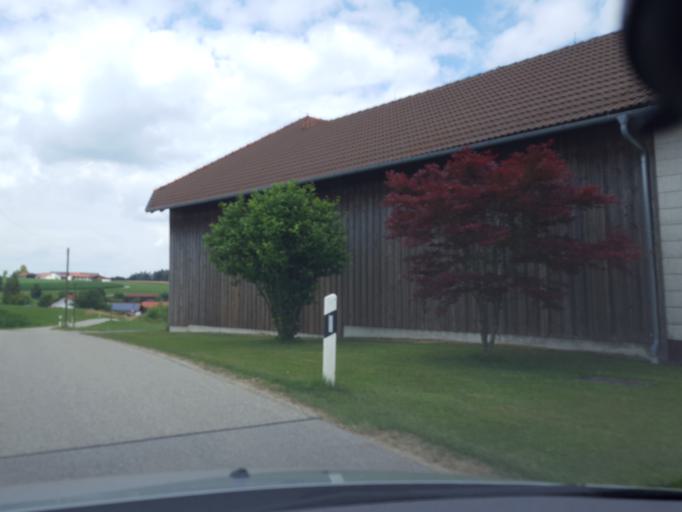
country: DE
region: Bavaria
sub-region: Upper Bavaria
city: Neumarkt-Sankt Veit
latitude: 48.3889
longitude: 12.4923
